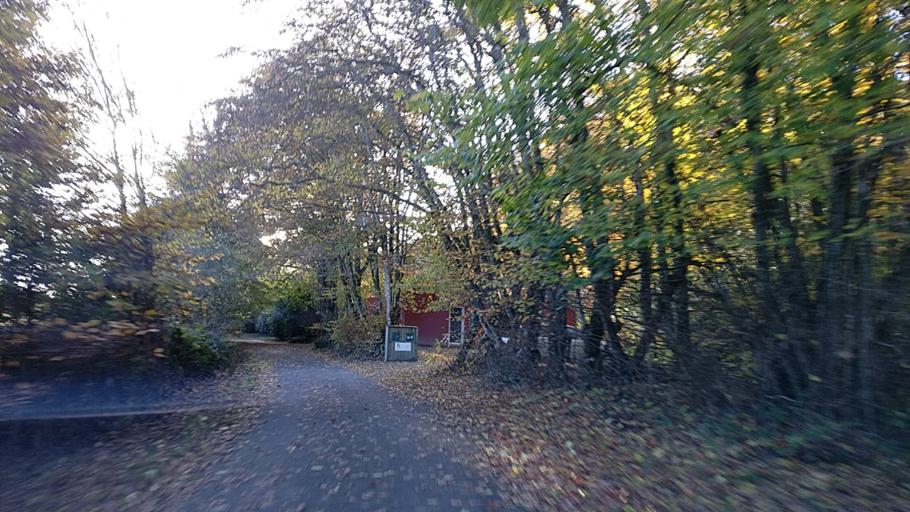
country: FR
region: Brittany
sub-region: Departement d'Ille-et-Vilaine
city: Acigne
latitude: 48.1694
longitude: -1.5361
